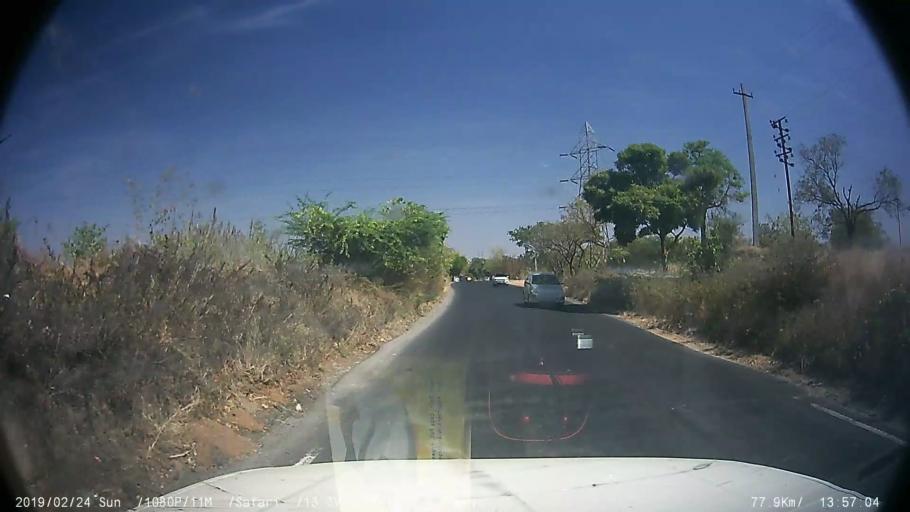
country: IN
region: Tamil Nadu
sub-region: Coimbatore
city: Sirumugai
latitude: 11.2655
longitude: 77.0216
